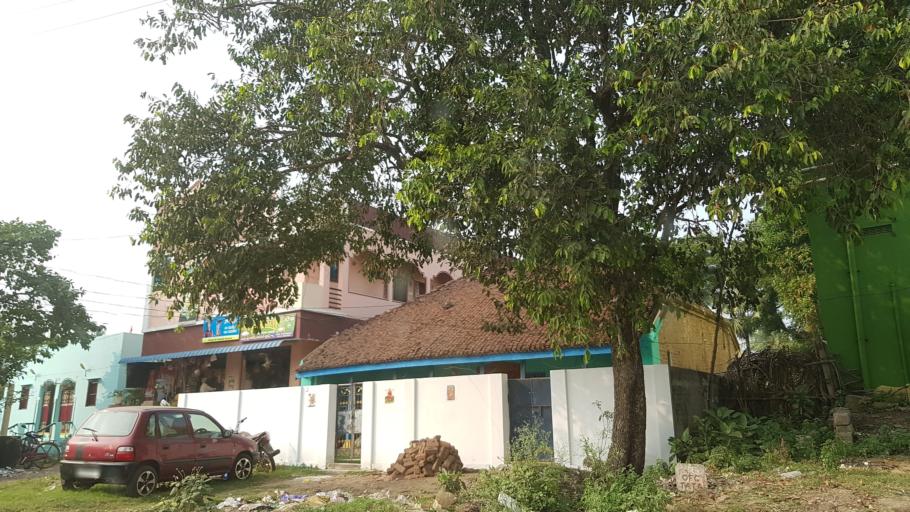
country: IN
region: Andhra Pradesh
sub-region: West Godavari
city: Akividu
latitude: 16.5373
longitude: 81.4071
